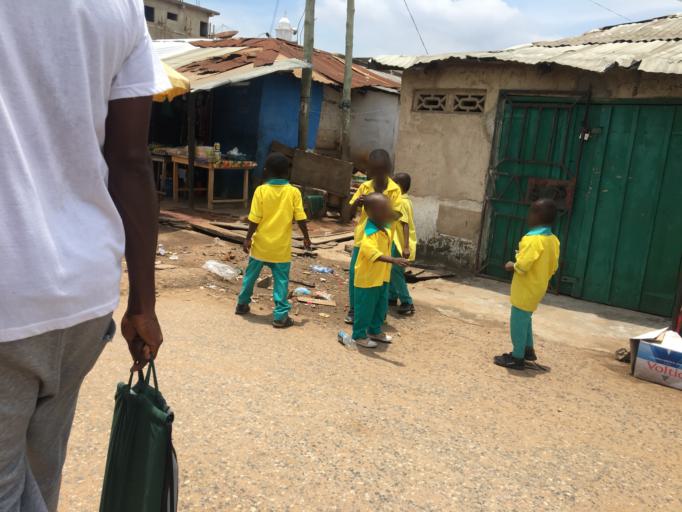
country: GH
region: Greater Accra
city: Accra
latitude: 5.5822
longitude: -0.1969
